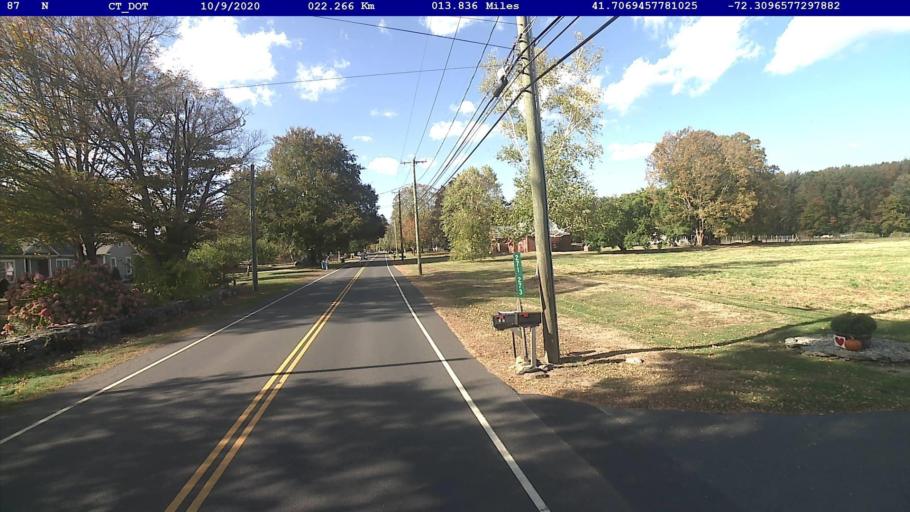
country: US
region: Connecticut
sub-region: Tolland County
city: South Coventry
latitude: 41.7070
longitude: -72.3097
